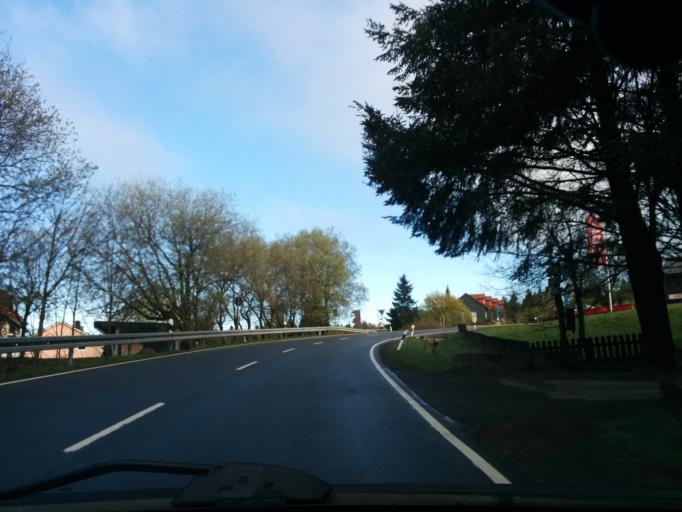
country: DE
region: Lower Saxony
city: Sankt Andreasberg
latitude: 51.7176
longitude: 10.5208
